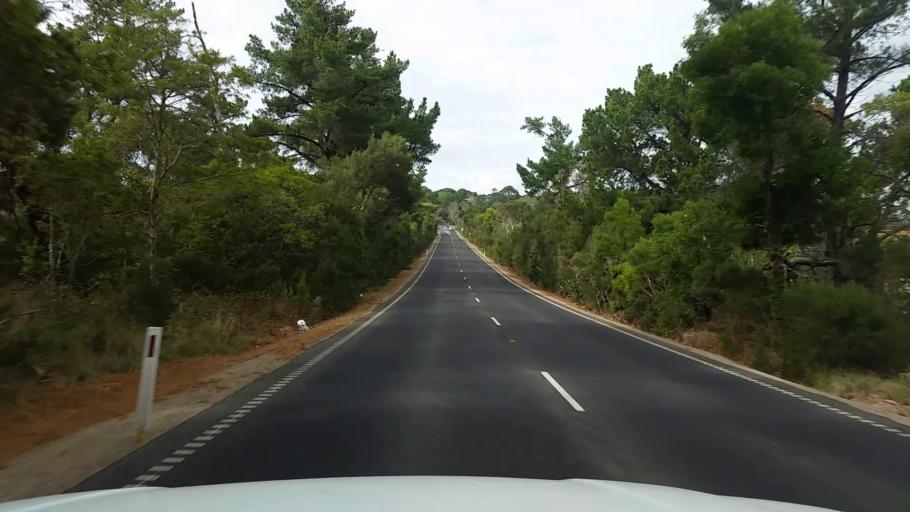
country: AU
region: Victoria
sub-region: Mornington Peninsula
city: Balnarring
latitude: -38.3599
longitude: 145.1131
